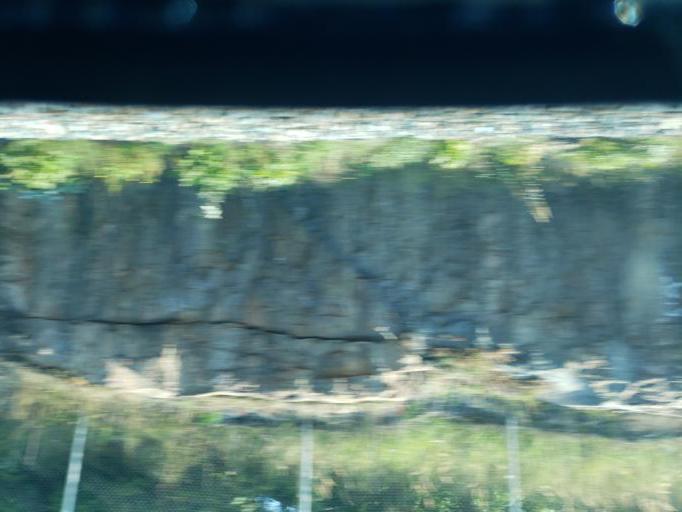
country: FI
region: Uusimaa
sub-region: Helsinki
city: Vantaa
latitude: 60.2458
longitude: 25.0009
